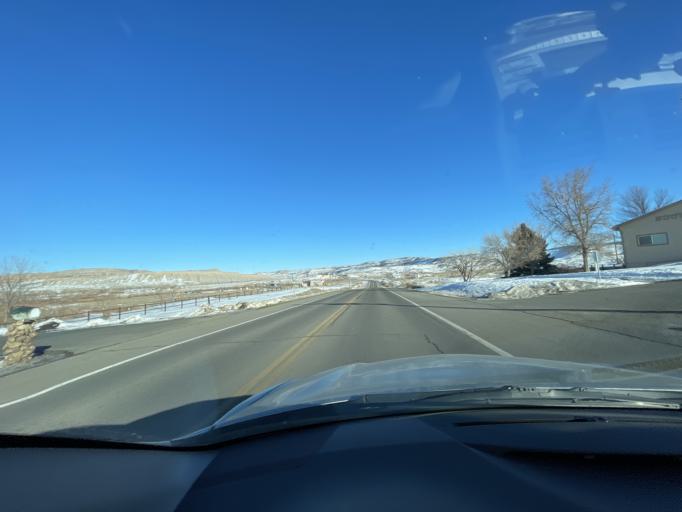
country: US
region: Colorado
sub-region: Rio Blanco County
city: Rangely
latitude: 40.0876
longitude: -108.7847
